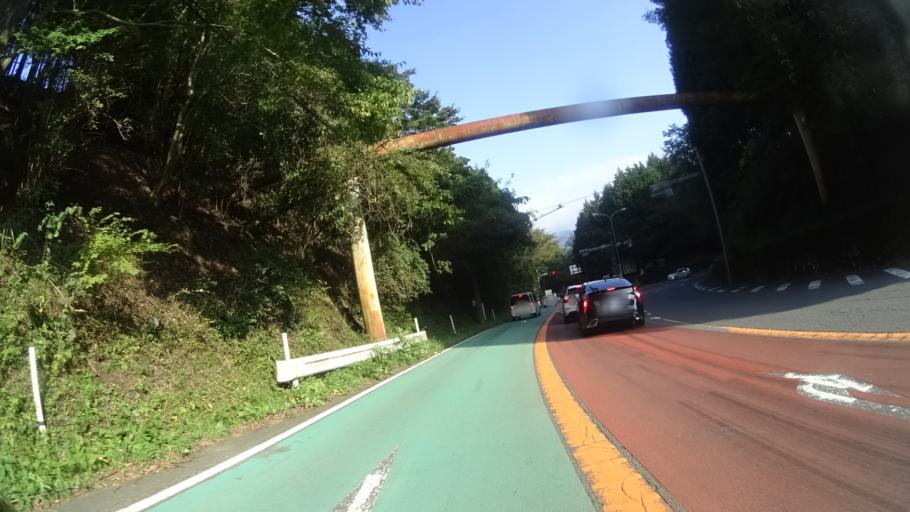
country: JP
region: Oita
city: Tsukawaki
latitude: 33.2619
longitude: 131.3243
